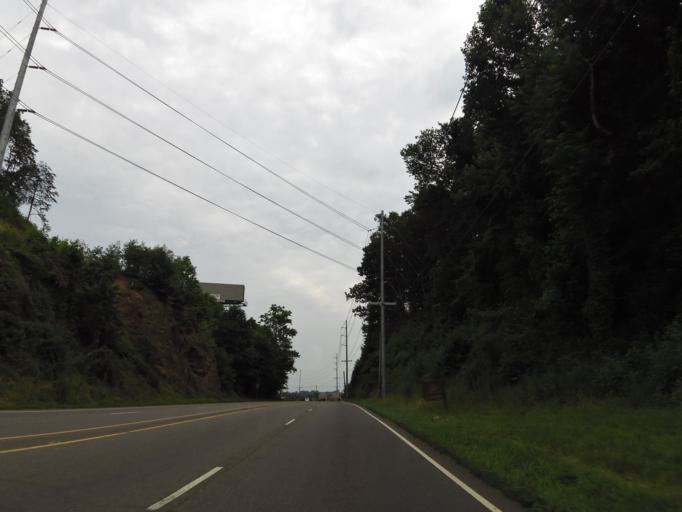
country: US
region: Tennessee
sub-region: Sevier County
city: Seymour
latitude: 35.8879
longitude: -83.7947
